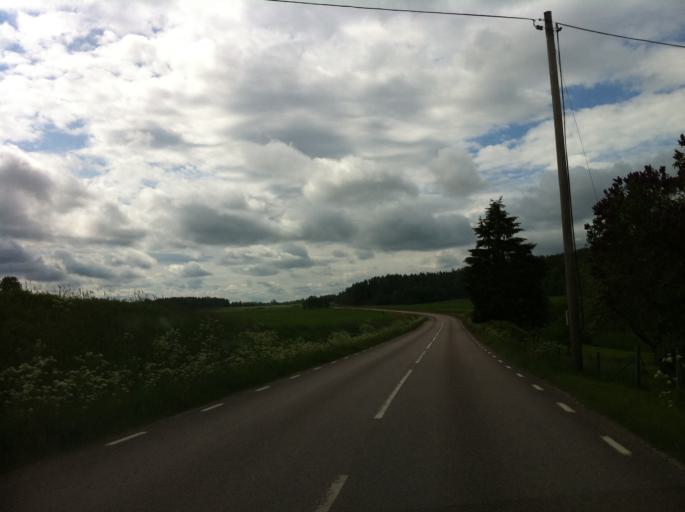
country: SE
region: Vaermland
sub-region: Sunne Kommun
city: Sunne
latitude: 59.9015
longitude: 13.1717
